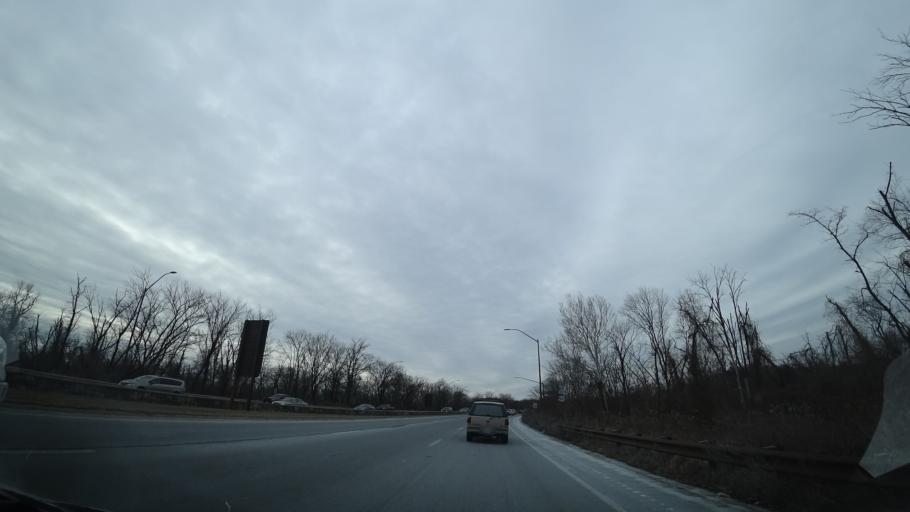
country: US
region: Maryland
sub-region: Prince George's County
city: Colmar Manor
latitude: 38.9187
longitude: -76.9391
